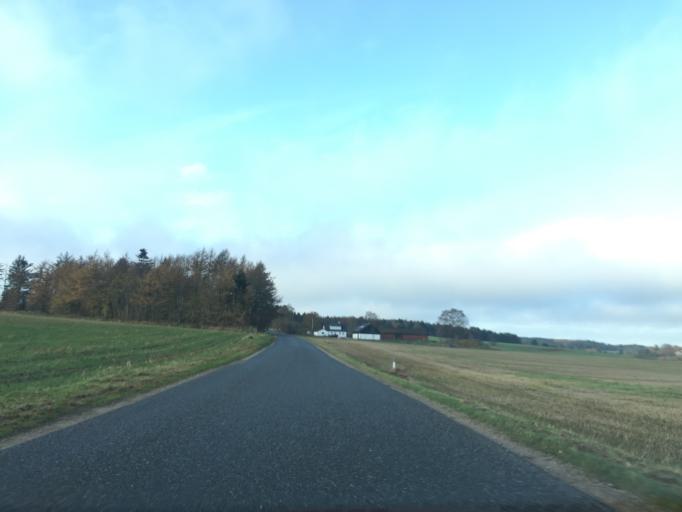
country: DK
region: Central Jutland
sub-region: Silkeborg Kommune
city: Svejbaek
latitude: 56.1953
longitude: 9.6901
